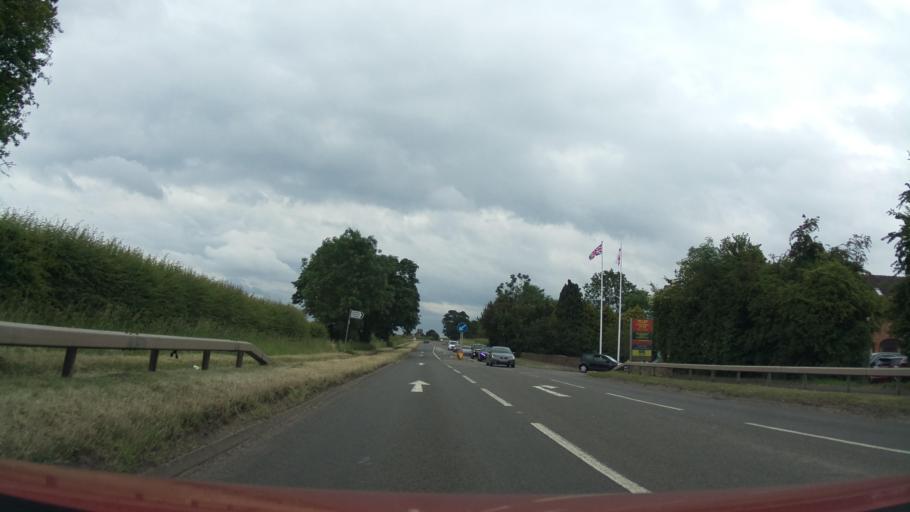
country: GB
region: England
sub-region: Staffordshire
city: Penkridge
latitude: 52.7473
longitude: -2.1073
